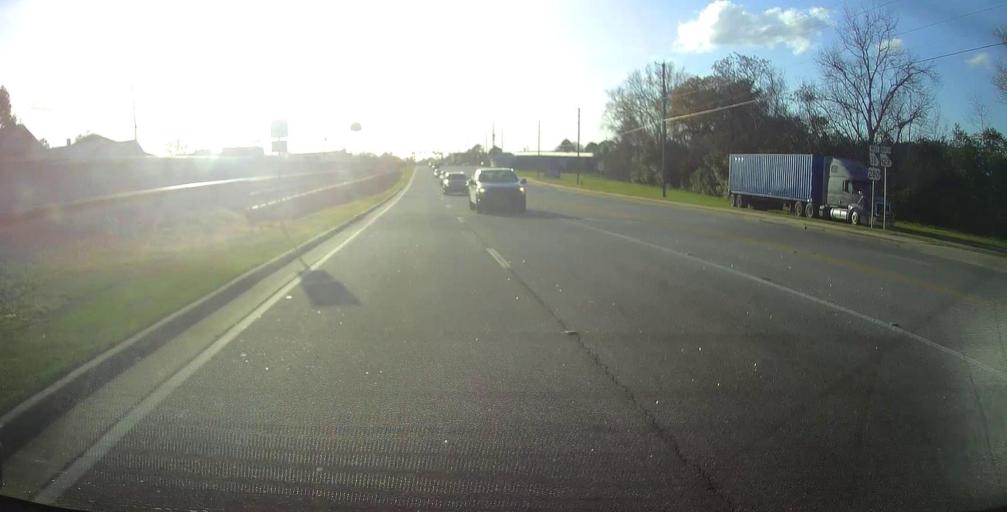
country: US
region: Georgia
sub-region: Evans County
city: Claxton
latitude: 32.1612
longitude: -81.9008
